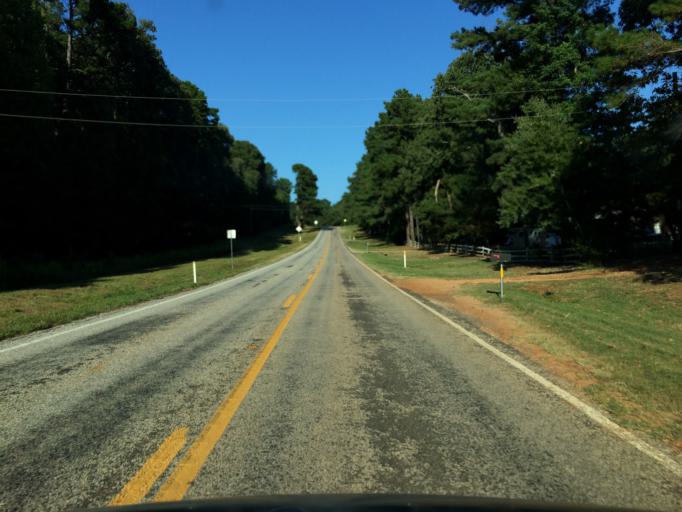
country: US
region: Texas
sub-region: Wood County
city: Hawkins
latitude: 32.6398
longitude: -95.2550
